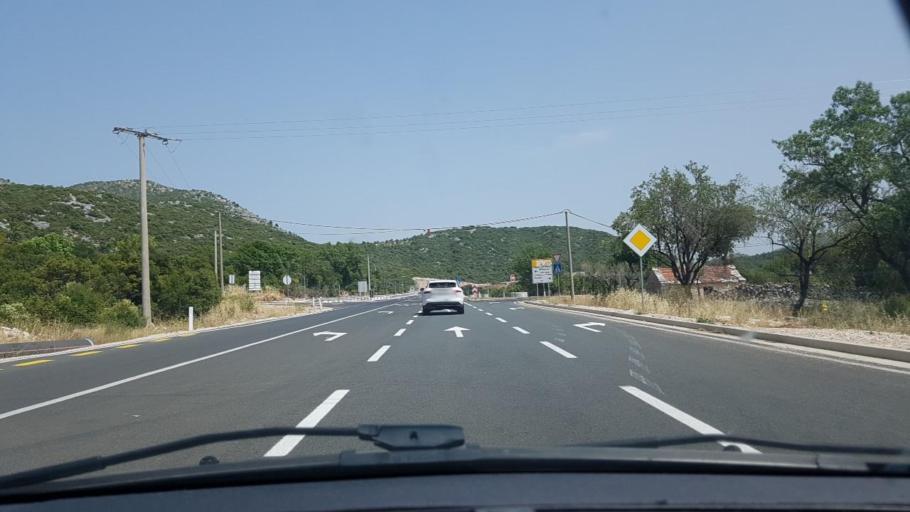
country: HR
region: Dubrovacko-Neretvanska
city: Ston
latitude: 42.9526
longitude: 17.7493
